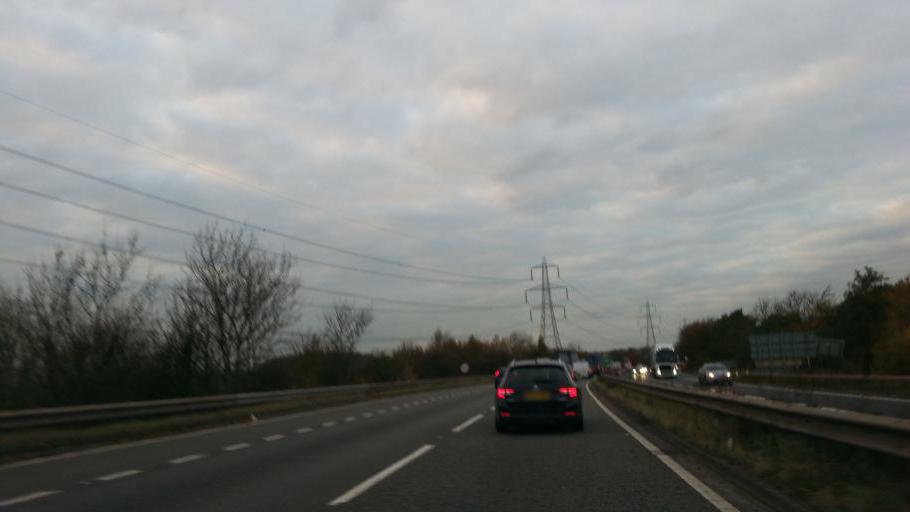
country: GB
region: England
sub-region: Lincolnshire
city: Grantham
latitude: 52.8984
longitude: -0.6658
